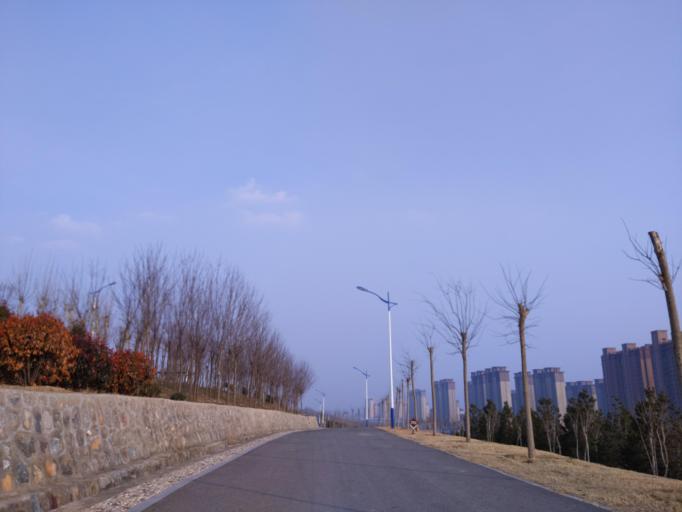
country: CN
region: Henan Sheng
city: Puyang
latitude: 35.8192
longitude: 115.0159
